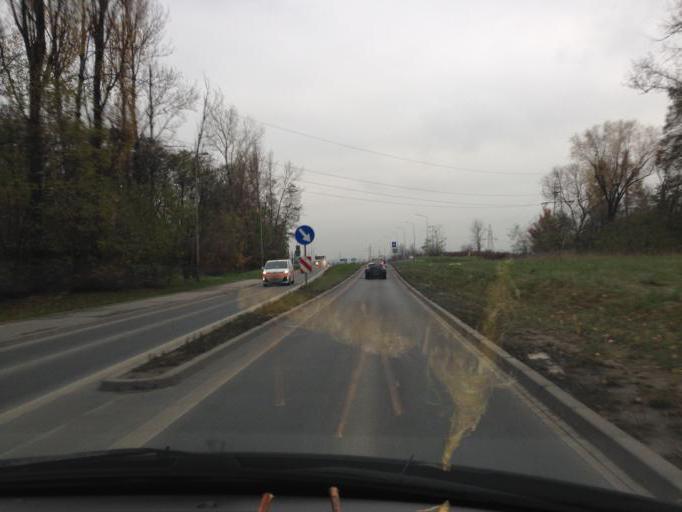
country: PL
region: Lesser Poland Voivodeship
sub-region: Powiat wielicki
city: Kokotow
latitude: 50.0722
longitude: 20.0643
